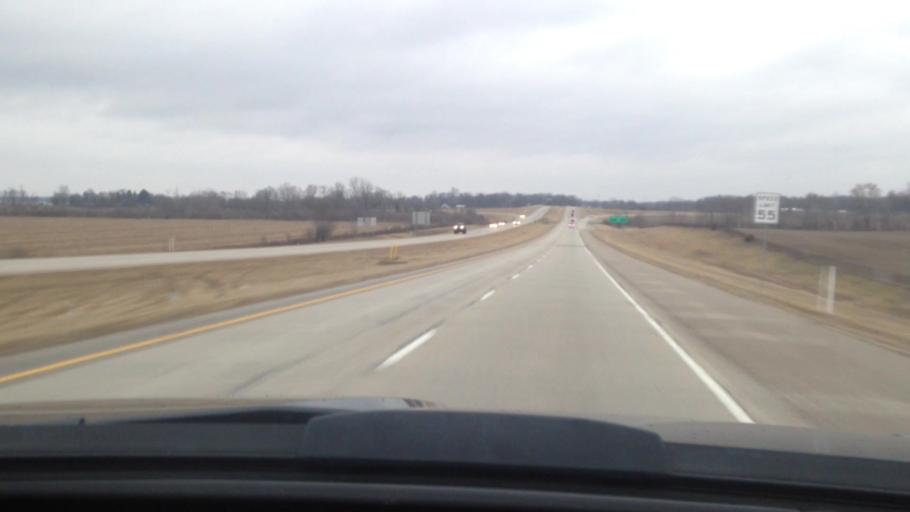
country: US
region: Indiana
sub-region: Delaware County
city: Muncie
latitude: 40.1877
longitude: -85.3365
